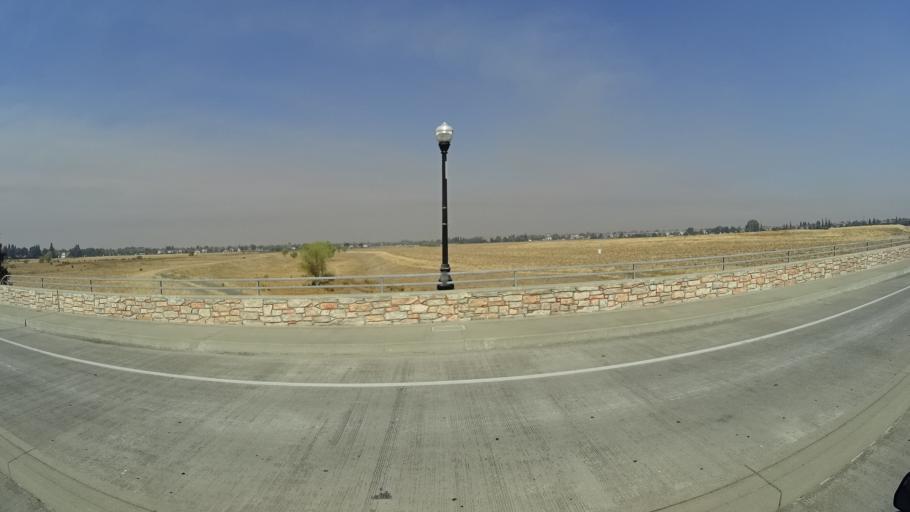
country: US
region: California
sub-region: Sacramento County
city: Laguna
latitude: 38.4328
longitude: -121.4092
